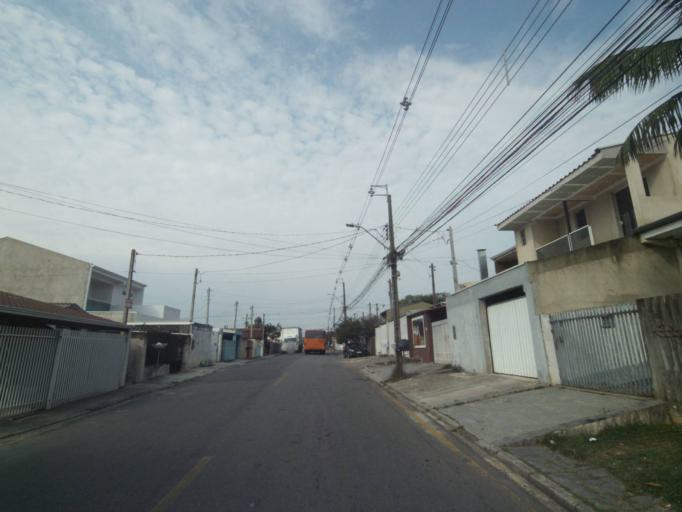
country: BR
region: Parana
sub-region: Pinhais
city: Pinhais
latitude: -25.4804
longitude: -49.2040
